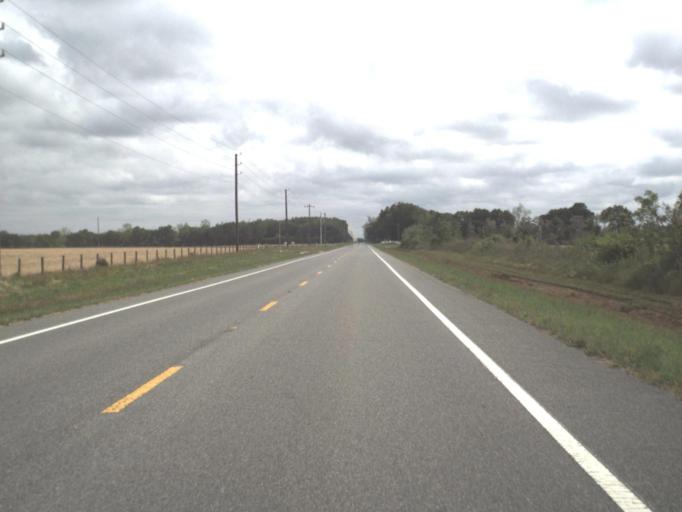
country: US
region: Florida
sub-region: Santa Rosa County
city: Point Baker
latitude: 30.7666
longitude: -87.0930
